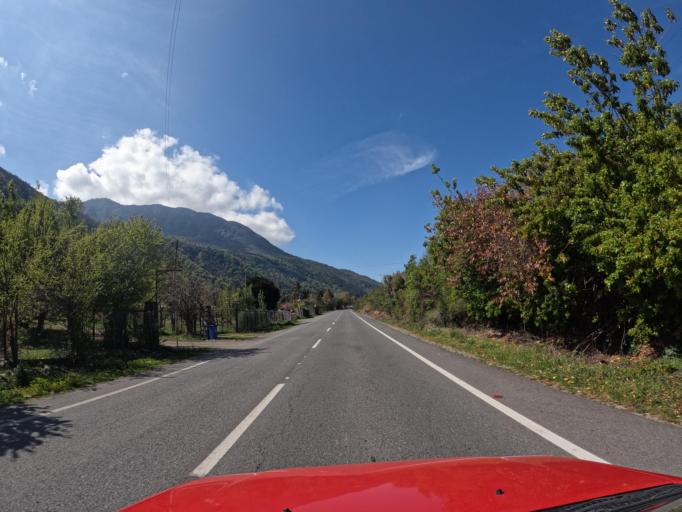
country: CL
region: Maule
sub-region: Provincia de Linares
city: Colbun
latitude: -35.7219
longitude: -71.1845
